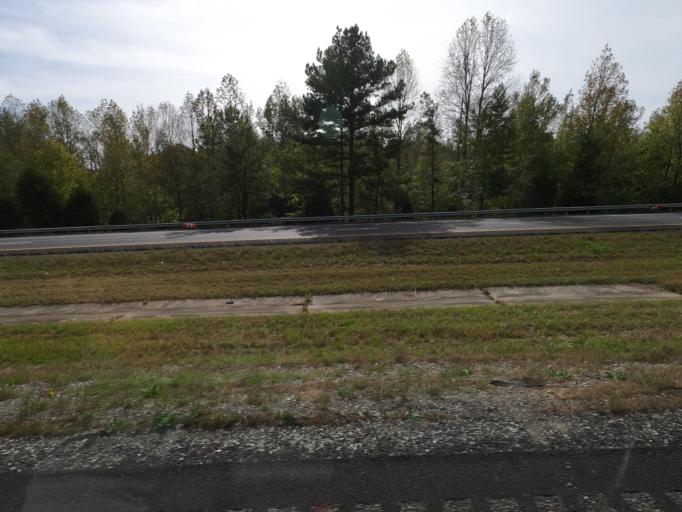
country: US
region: Tennessee
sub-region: Decatur County
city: Parsons
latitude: 35.8189
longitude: -88.1465
